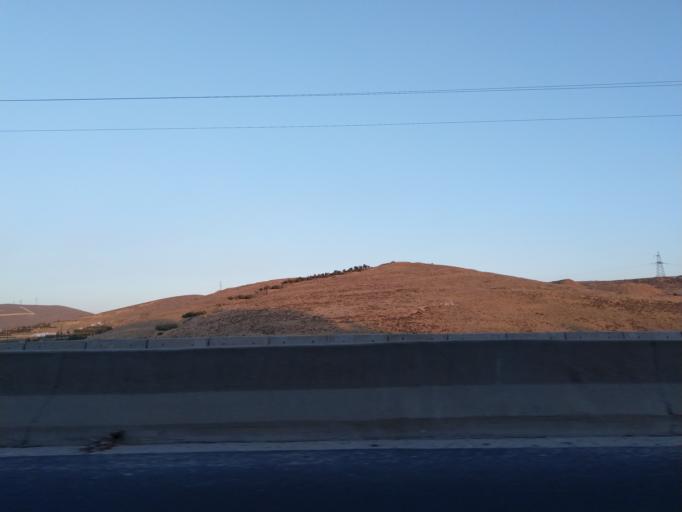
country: SY
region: Rif-dimashq
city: At Tall
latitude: 33.5882
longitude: 36.3081
